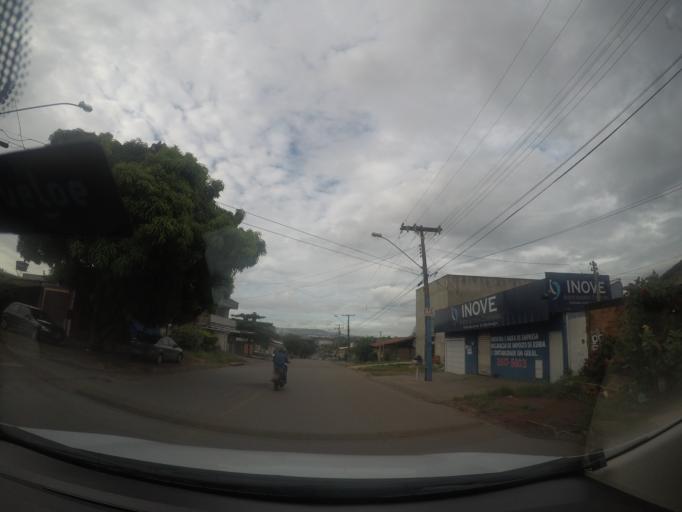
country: BR
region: Goias
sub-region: Goiania
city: Goiania
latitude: -16.6225
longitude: -49.3272
